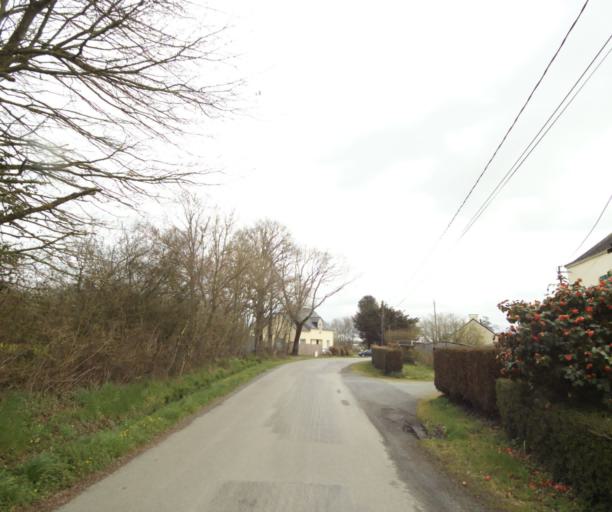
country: FR
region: Pays de la Loire
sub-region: Departement de la Loire-Atlantique
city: Bouvron
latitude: 47.4255
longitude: -1.8633
